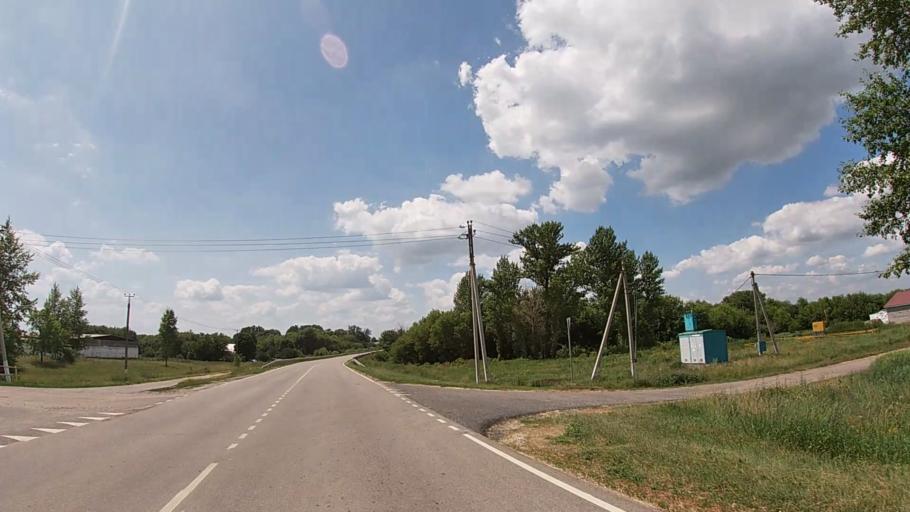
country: RU
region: Belgorod
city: Grayvoron
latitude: 50.4368
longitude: 35.6053
